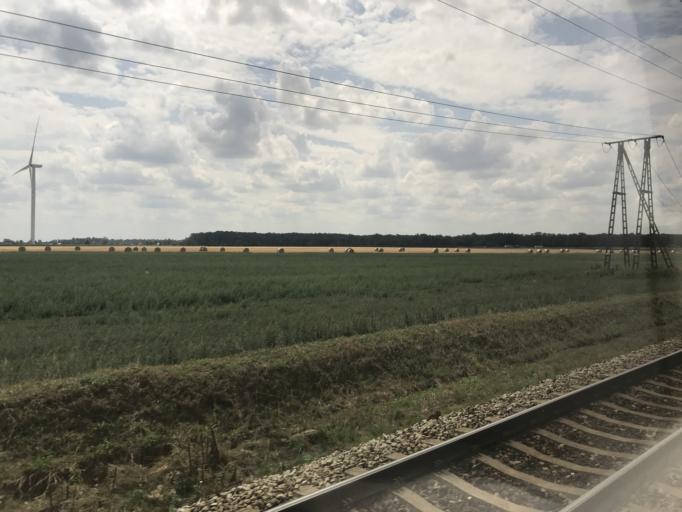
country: PL
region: Greater Poland Voivodeship
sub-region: Powiat nowotomyski
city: Opalenica
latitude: 52.3246
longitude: 16.4591
